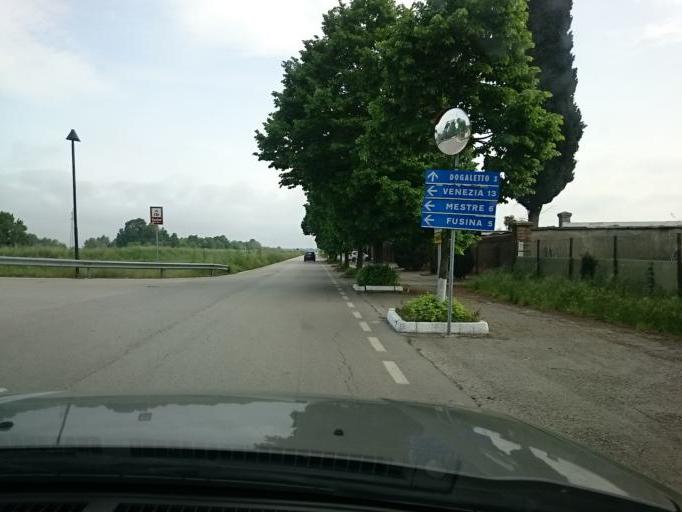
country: IT
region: Veneto
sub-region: Provincia di Venezia
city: Mestre
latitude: 45.4337
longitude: 12.2021
